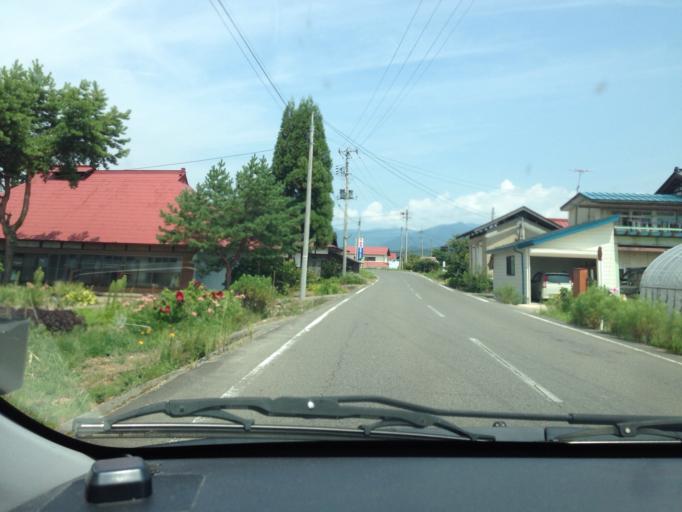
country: JP
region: Fukushima
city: Kitakata
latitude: 37.6731
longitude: 139.8803
